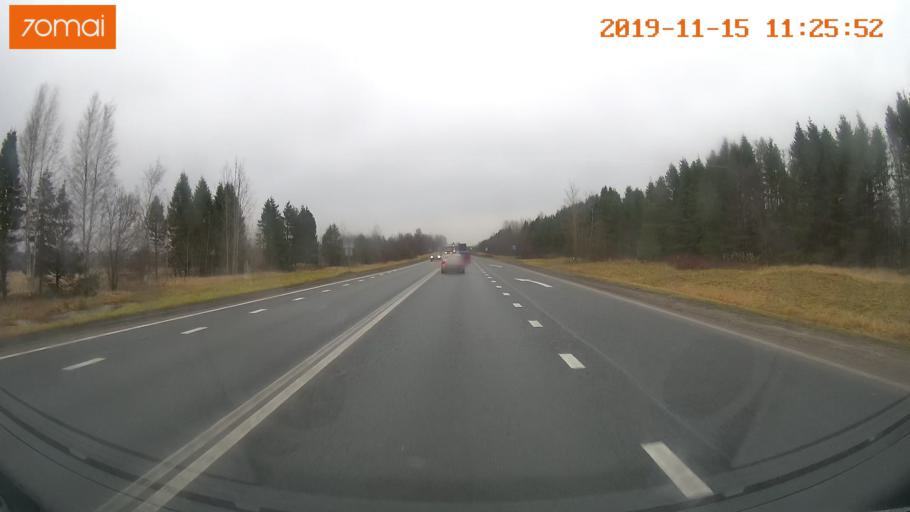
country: RU
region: Vologda
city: Molochnoye
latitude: 59.1642
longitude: 39.4341
